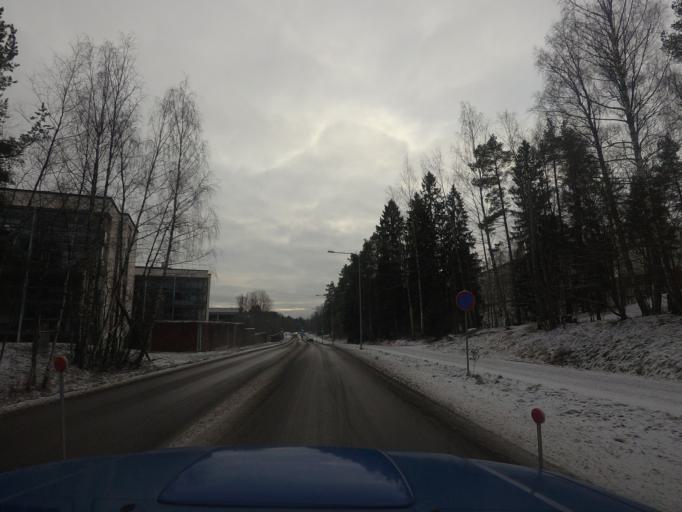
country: FI
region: Uusimaa
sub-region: Helsinki
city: Kilo
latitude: 60.2326
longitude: 24.7735
